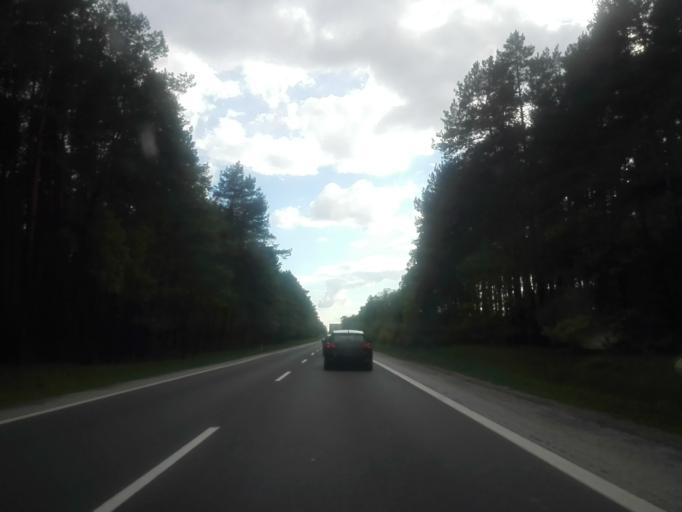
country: PL
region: Masovian Voivodeship
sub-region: Powiat ostrowski
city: Brok
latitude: 52.7303
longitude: 21.7336
